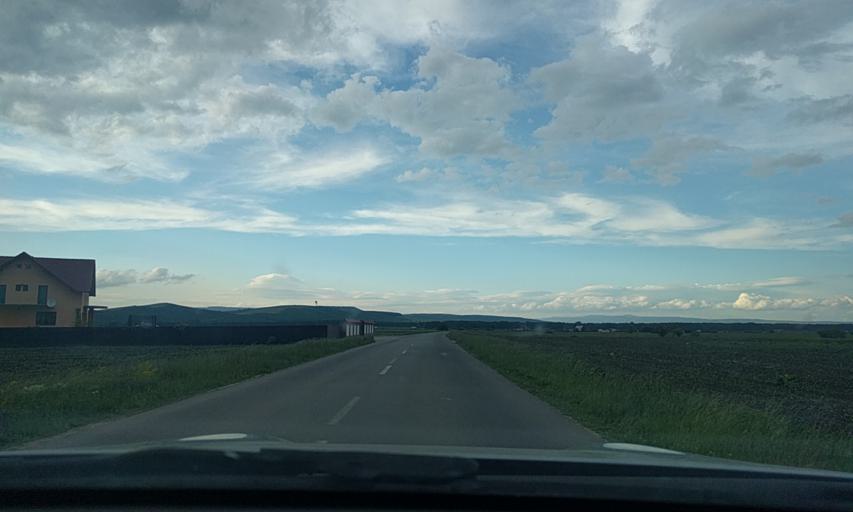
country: RO
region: Brasov
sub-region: Comuna Harman
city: Harman
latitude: 45.7275
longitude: 25.6991
